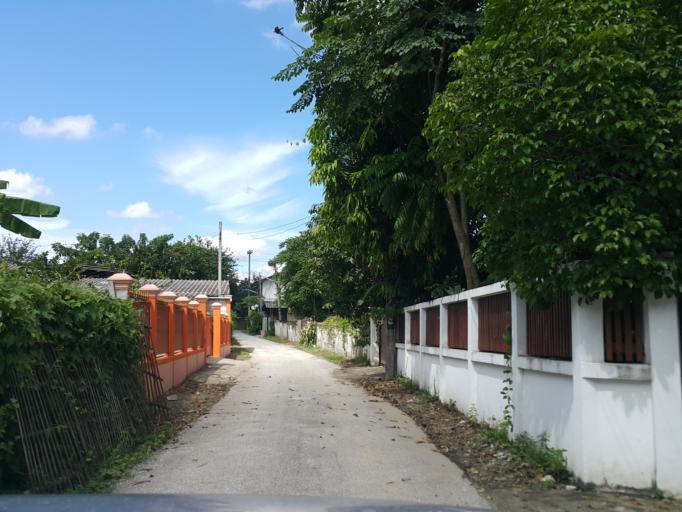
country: TH
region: Chiang Mai
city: San Kamphaeng
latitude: 18.7569
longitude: 99.1259
